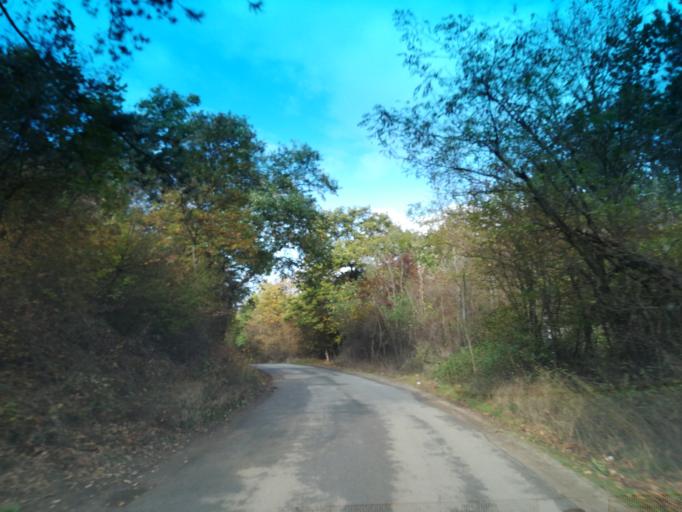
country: BG
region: Stara Zagora
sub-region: Obshtina Nikolaevo
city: Elkhovo
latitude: 42.3216
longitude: 25.4013
